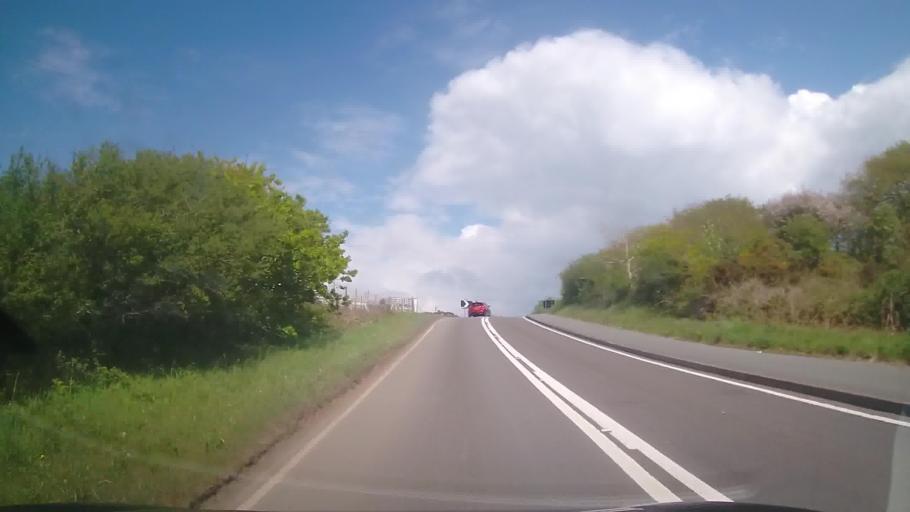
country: GB
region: Wales
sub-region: Gwynedd
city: Porthmadog
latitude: 52.9175
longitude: -4.1500
